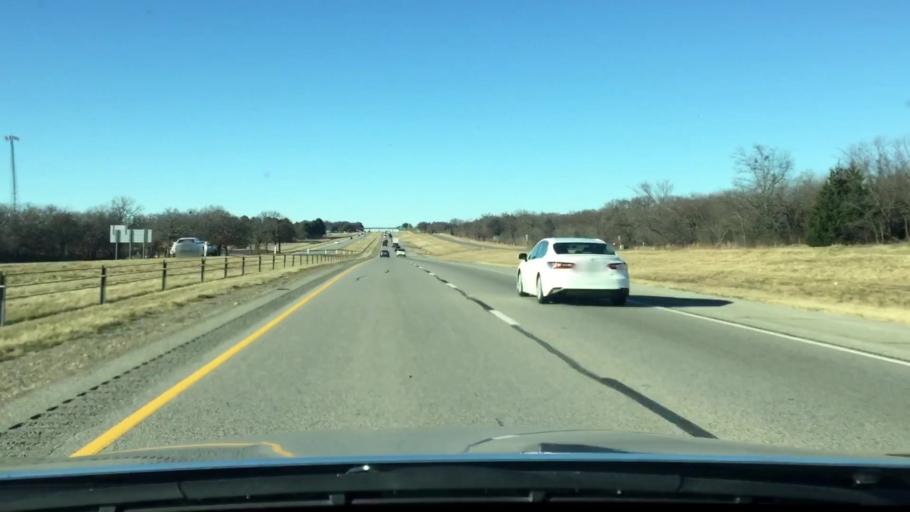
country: US
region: Texas
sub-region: Johnson County
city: Alvarado
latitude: 32.3691
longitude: -97.2018
